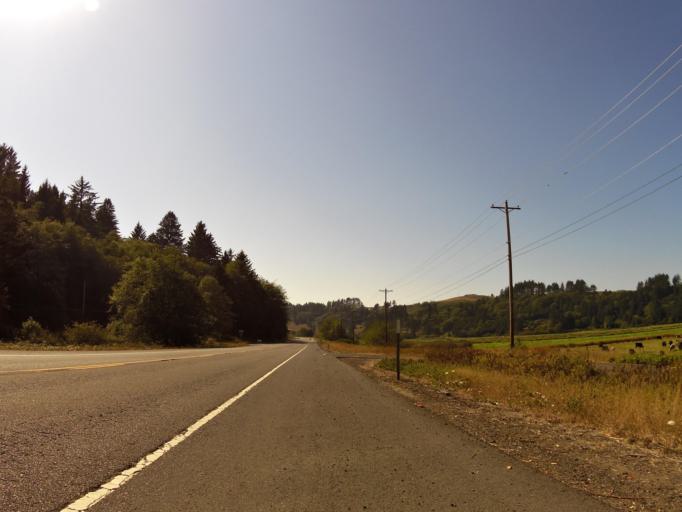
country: US
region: Oregon
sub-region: Tillamook County
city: Pacific City
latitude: 45.1608
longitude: -123.9396
